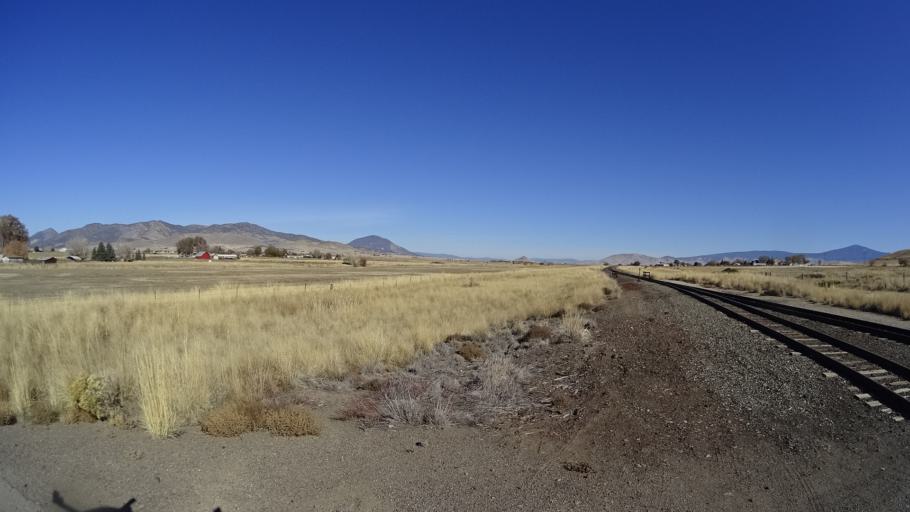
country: US
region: California
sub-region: Siskiyou County
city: Montague
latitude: 41.7347
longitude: -122.5220
